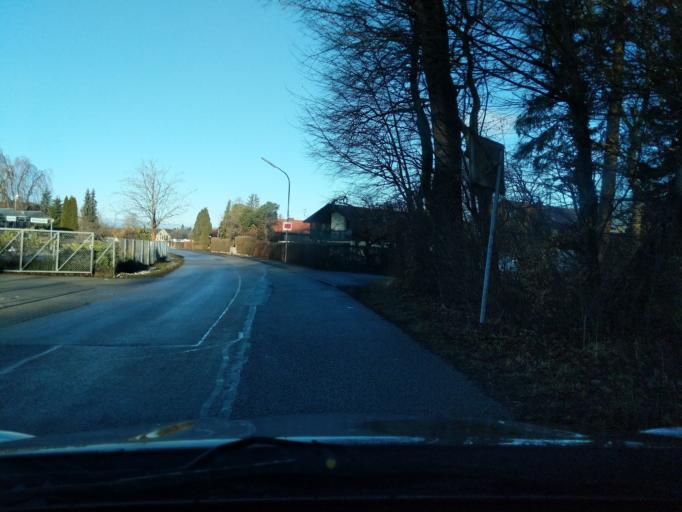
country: DE
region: Bavaria
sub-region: Upper Bavaria
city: Zorneding
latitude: 48.0900
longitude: 11.8449
